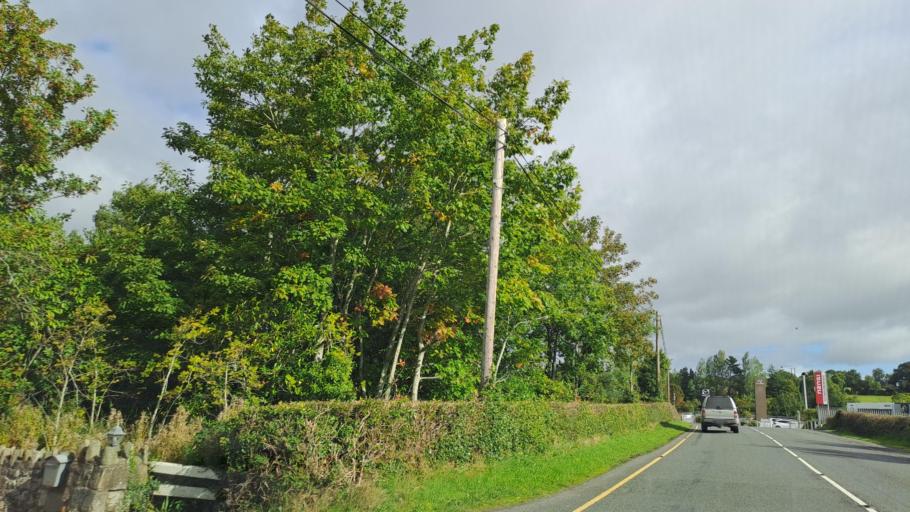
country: IE
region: Ulster
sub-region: County Monaghan
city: Carrickmacross
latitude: 53.9494
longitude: -6.7609
